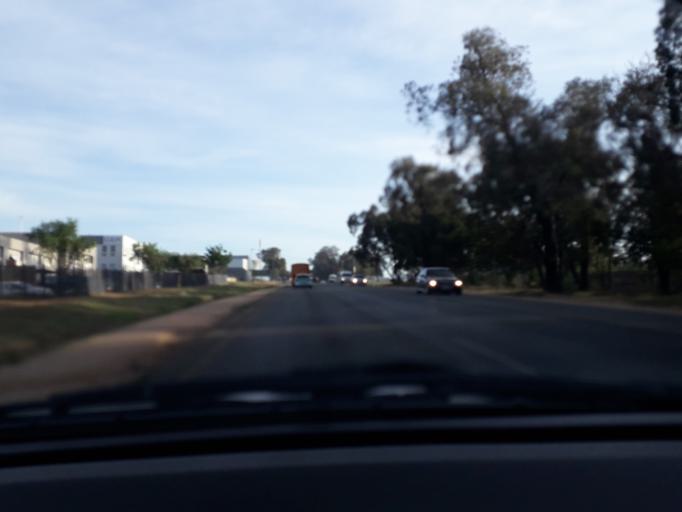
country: ZA
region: Gauteng
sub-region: City of Johannesburg Metropolitan Municipality
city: Midrand
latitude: -25.9455
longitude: 28.1433
